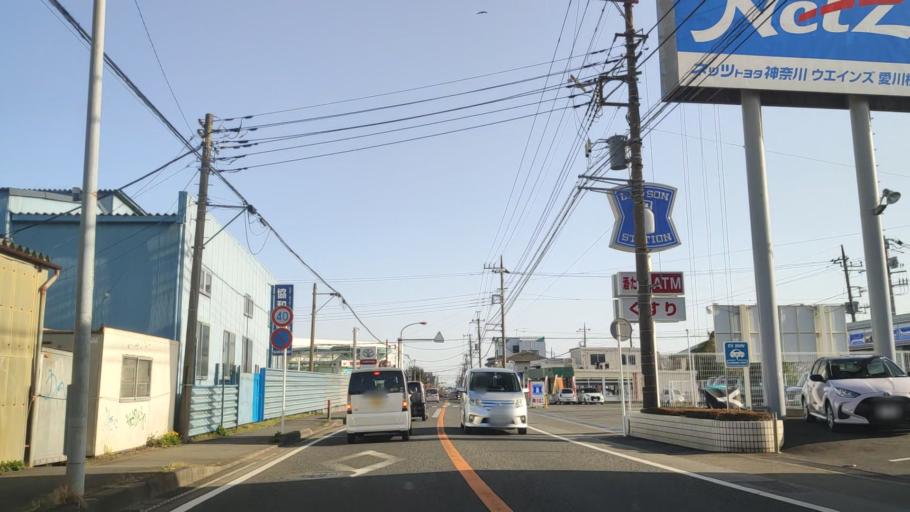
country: JP
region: Kanagawa
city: Zama
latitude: 35.5126
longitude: 139.3379
